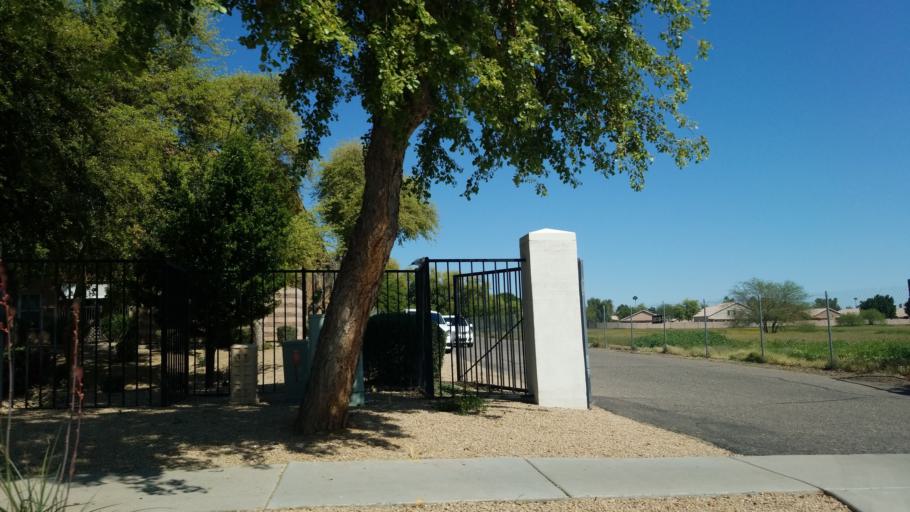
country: US
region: Arizona
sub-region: Maricopa County
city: Glendale
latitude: 33.5517
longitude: -112.1732
